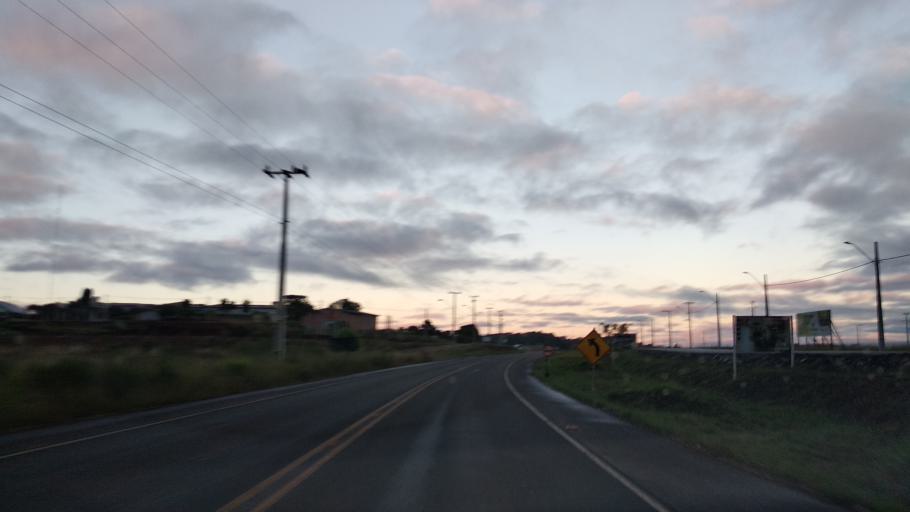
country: BR
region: Santa Catarina
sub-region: Campos Novos
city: Campos Novos
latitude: -27.3768
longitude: -51.2055
